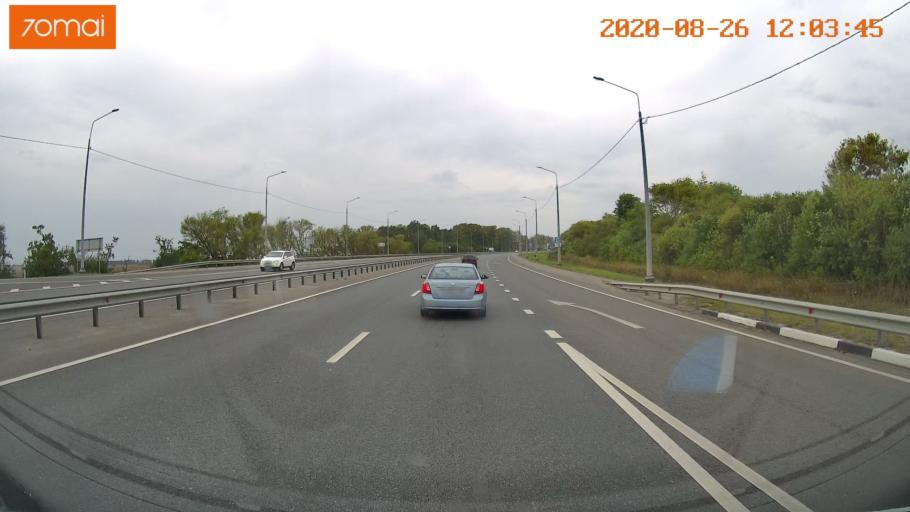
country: RU
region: Rjazan
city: Kiritsy
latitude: 54.3031
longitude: 40.2000
